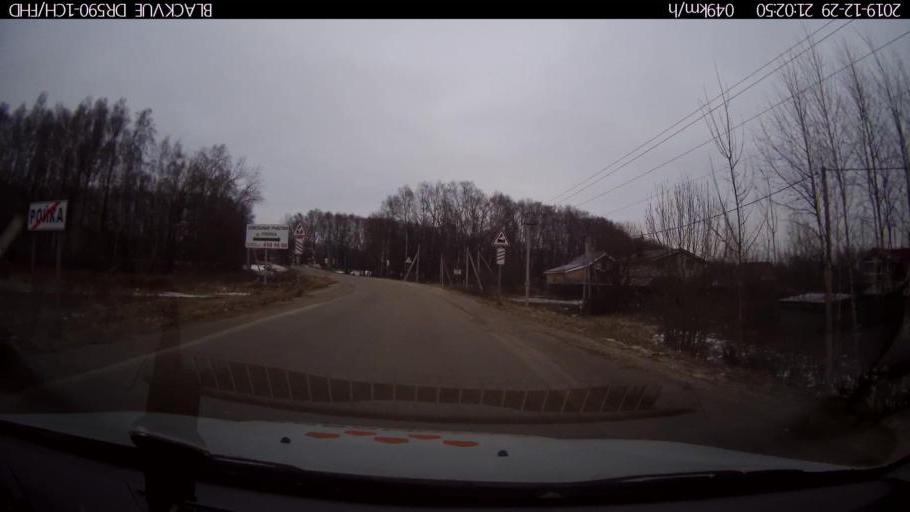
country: RU
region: Nizjnij Novgorod
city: Afonino
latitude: 56.1929
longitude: 44.0040
